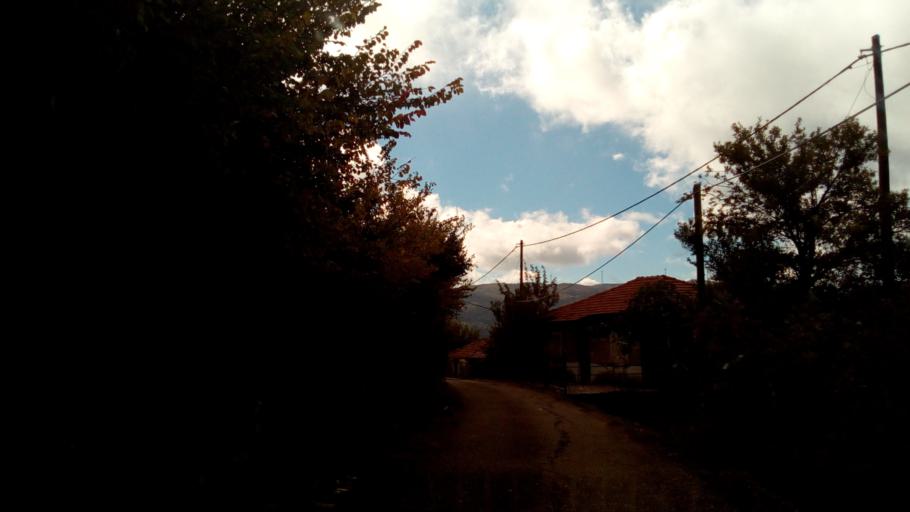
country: GR
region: West Greece
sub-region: Nomos Aitolias kai Akarnanias
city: Nafpaktos
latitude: 38.4995
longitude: 21.8420
